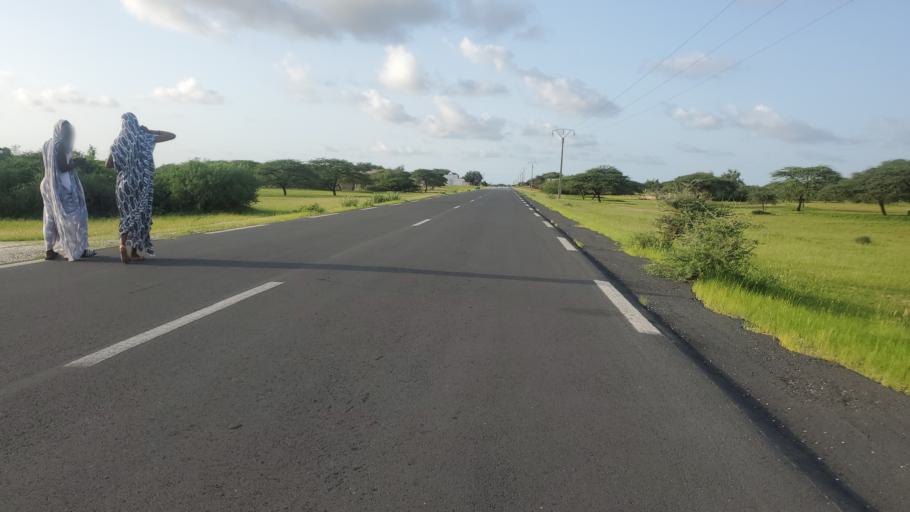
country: SN
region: Saint-Louis
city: Saint-Louis
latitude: 16.1498
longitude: -16.4097
